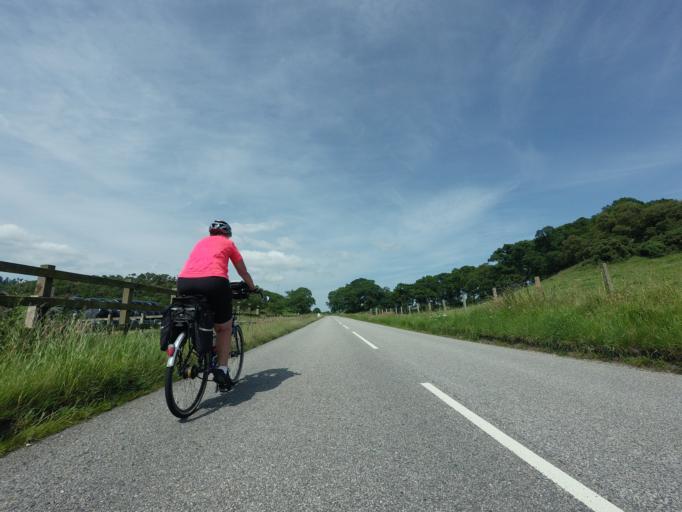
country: GB
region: Scotland
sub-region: Highland
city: Tain
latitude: 57.8499
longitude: -4.2034
